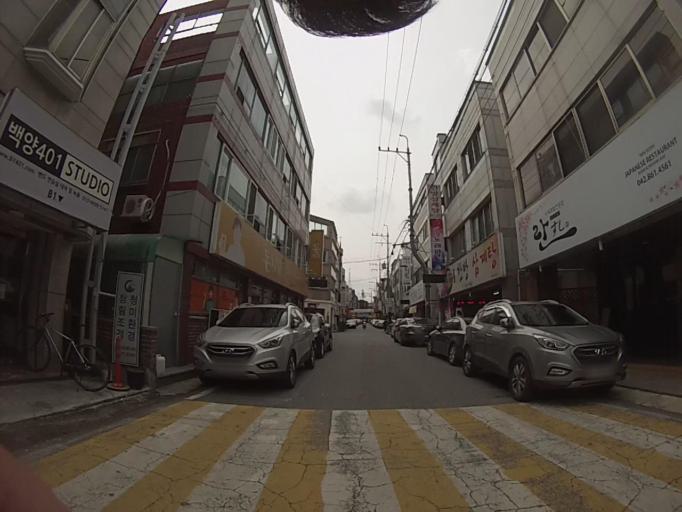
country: KR
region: Daejeon
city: Songgang-dong
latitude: 36.3637
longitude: 127.3583
